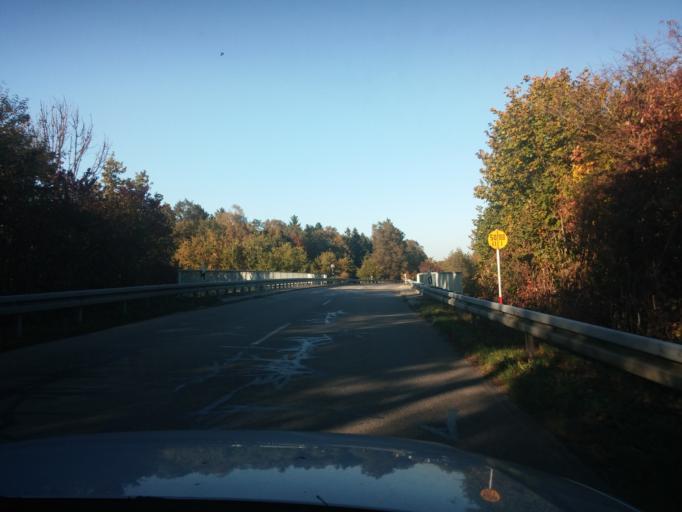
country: DE
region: Bavaria
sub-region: Upper Bavaria
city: Forstinning
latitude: 48.1806
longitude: 11.9182
